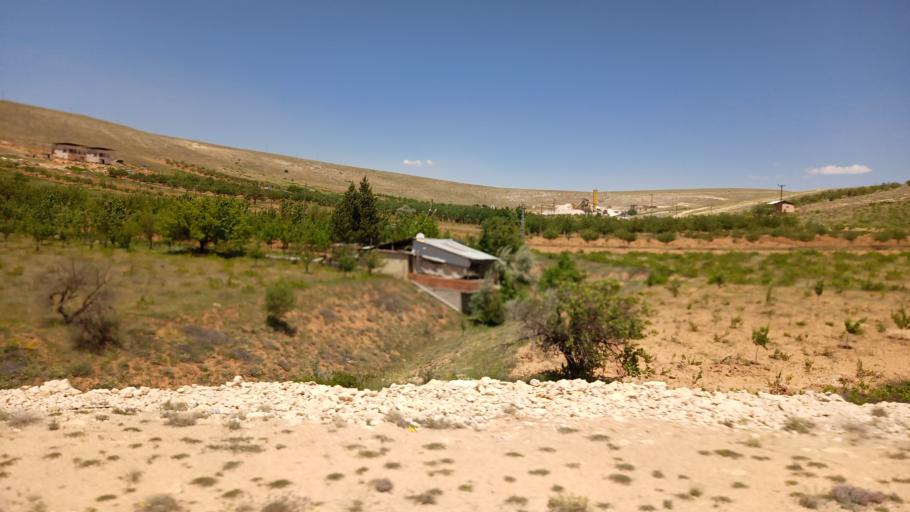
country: TR
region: Malatya
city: Darende
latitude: 38.6011
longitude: 37.4648
